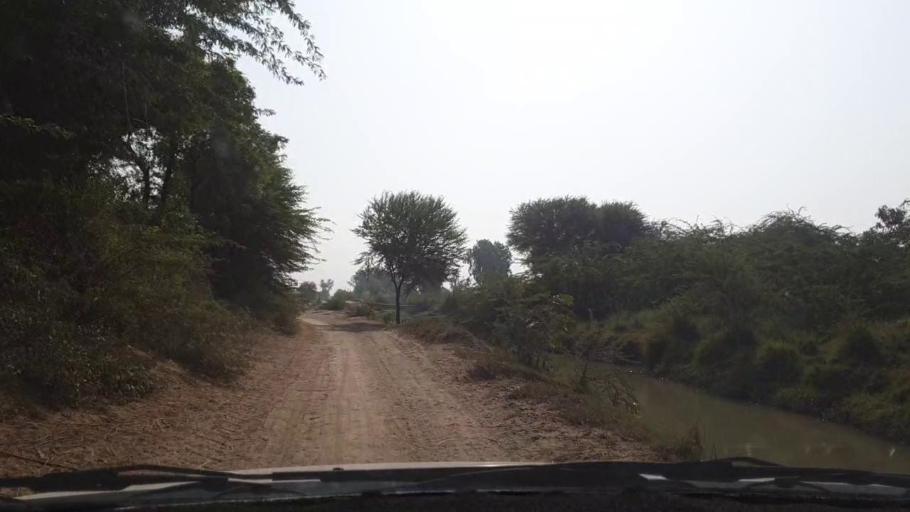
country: PK
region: Sindh
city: Tando Muhammad Khan
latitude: 25.0799
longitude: 68.3611
